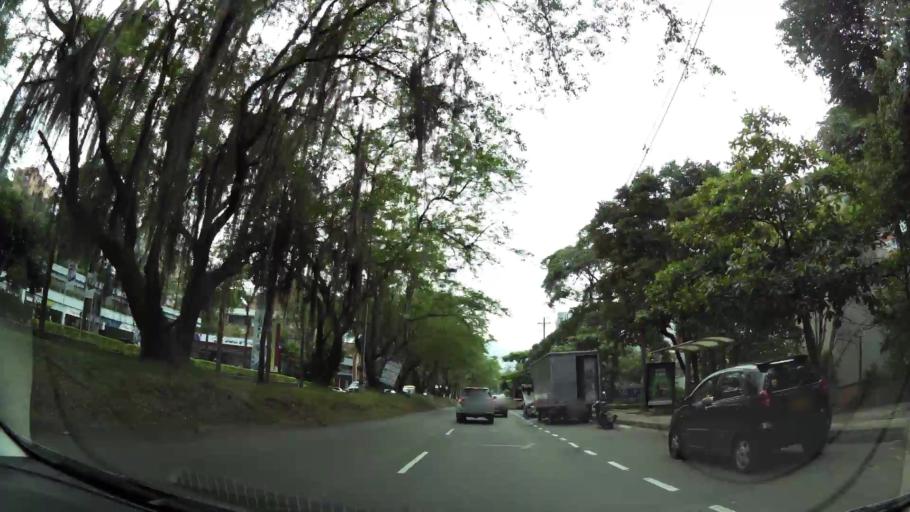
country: CO
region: Antioquia
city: Envigado
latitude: 6.1854
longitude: -75.5788
